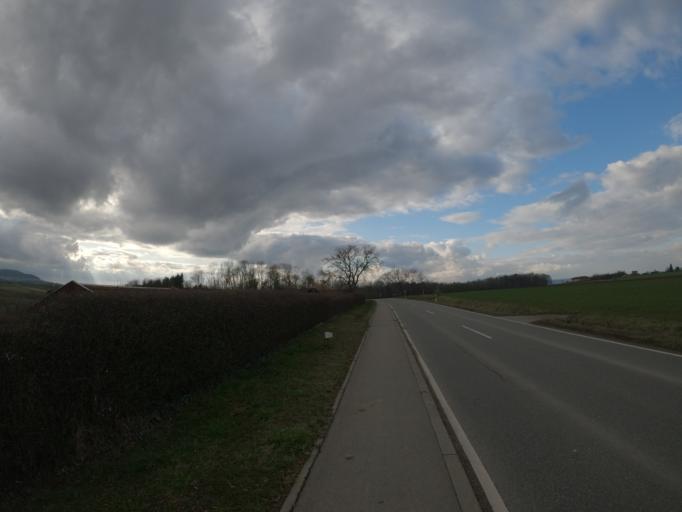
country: DE
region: Baden-Wuerttemberg
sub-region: Regierungsbezirk Stuttgart
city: Heiningen
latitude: 48.6611
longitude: 9.6344
